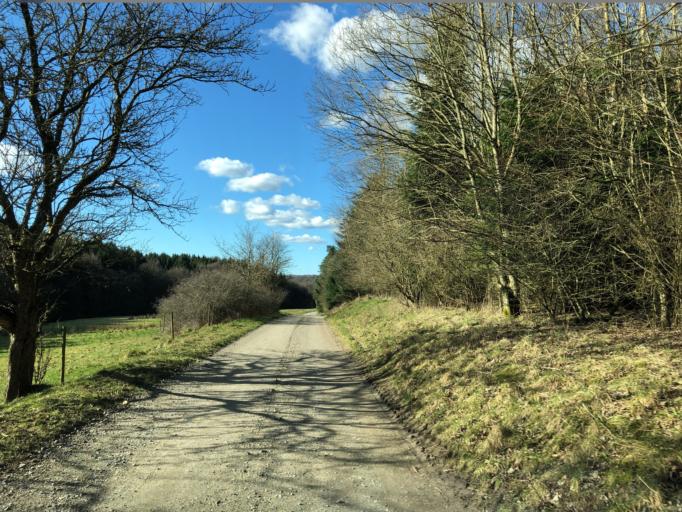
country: DK
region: Central Jutland
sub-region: Favrskov Kommune
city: Hammel
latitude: 56.3110
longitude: 9.9148
